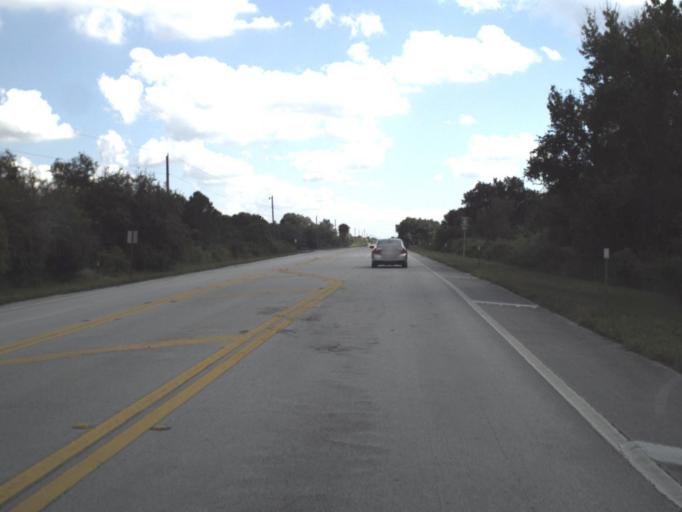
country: US
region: Florida
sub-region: Highlands County
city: Lake Placid
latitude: 27.4010
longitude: -81.1662
